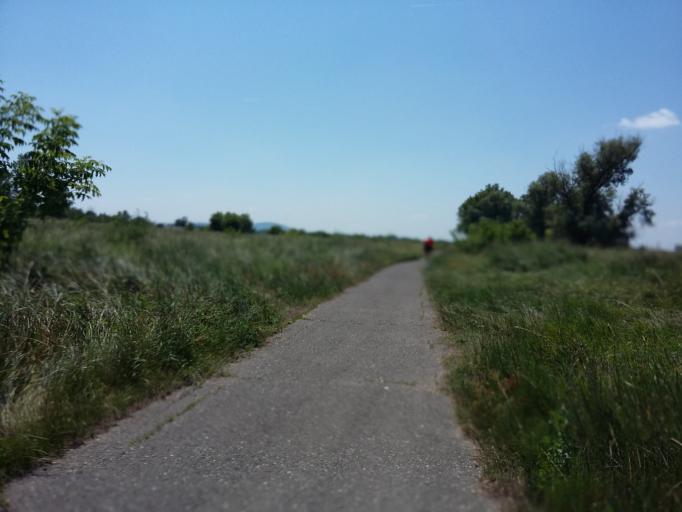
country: AT
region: Lower Austria
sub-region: Politischer Bezirk Ganserndorf
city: Marchegg
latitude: 48.2626
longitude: 16.9579
